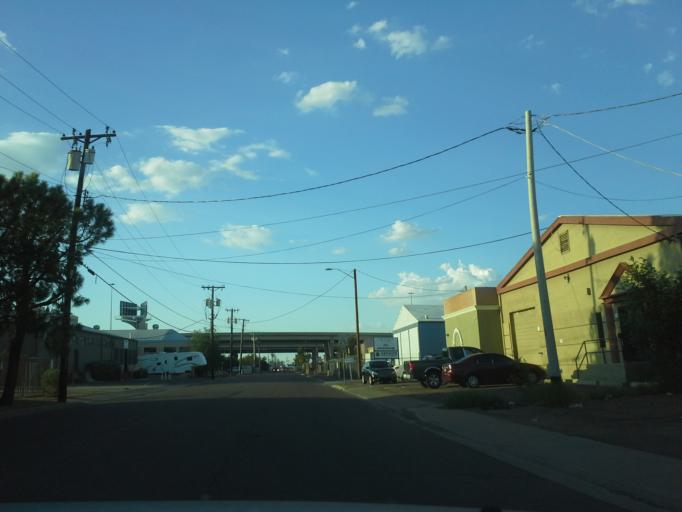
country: US
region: Arizona
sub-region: Maricopa County
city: Phoenix
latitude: 33.4585
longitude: -112.1044
